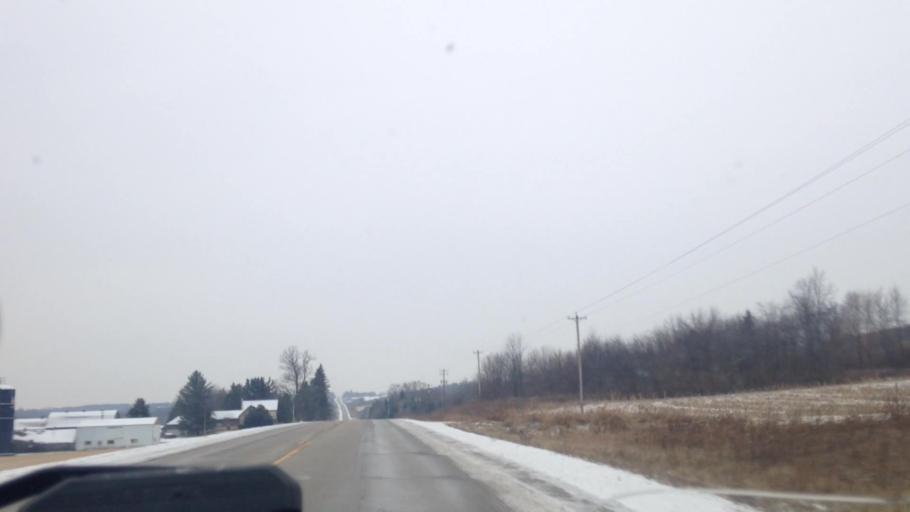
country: US
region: Wisconsin
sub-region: Dodge County
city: Hustisford
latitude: 43.2894
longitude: -88.5187
